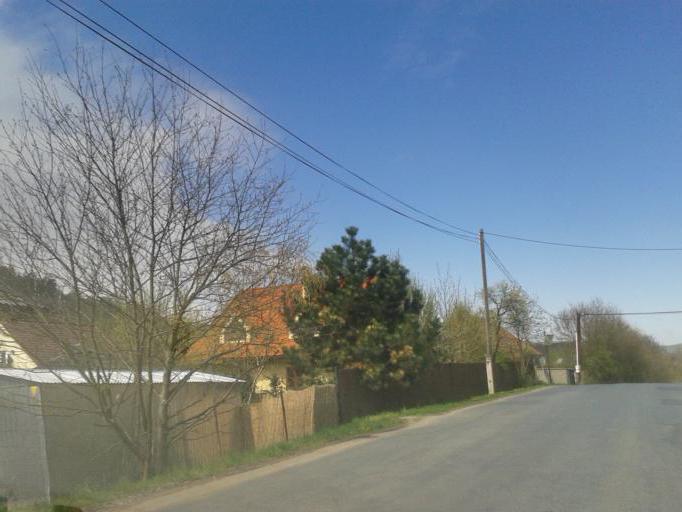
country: CZ
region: Central Bohemia
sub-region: Okres Beroun
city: Lodenice
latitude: 50.0006
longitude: 14.1590
